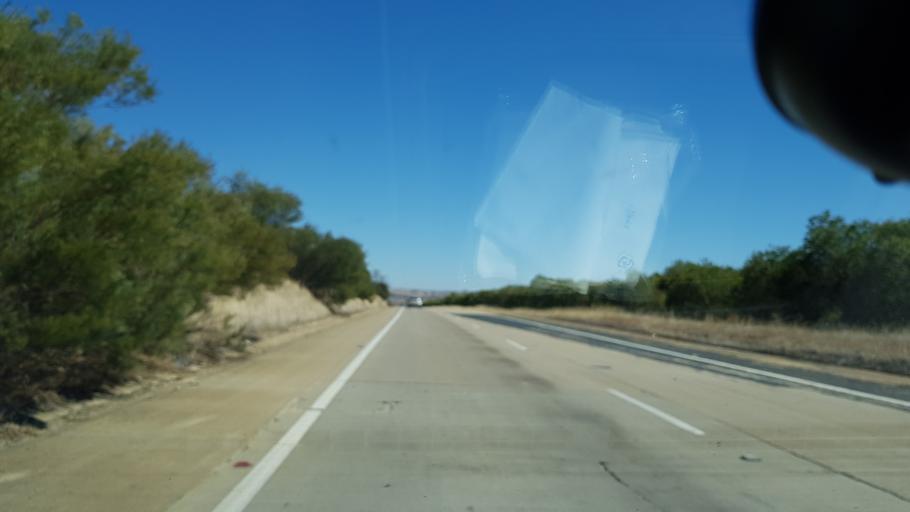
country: AU
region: New South Wales
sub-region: Gundagai
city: Gundagai
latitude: -34.8161
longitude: 148.3996
